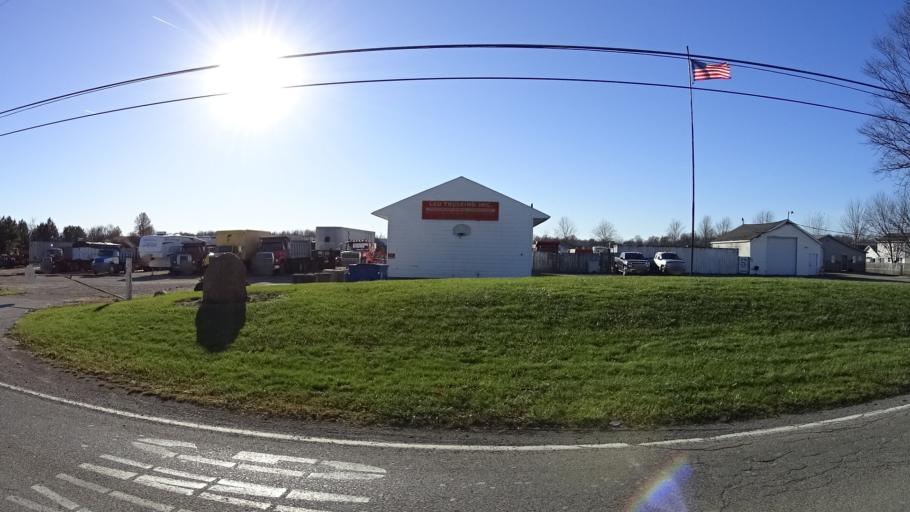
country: US
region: Ohio
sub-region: Lorain County
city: Elyria
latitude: 41.3545
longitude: -82.1405
